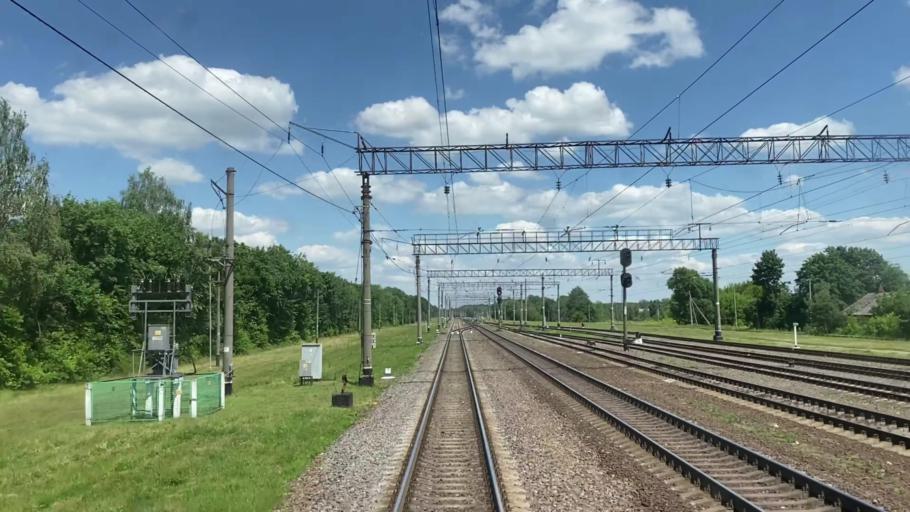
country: BY
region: Brest
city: Zhabinka
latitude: 52.2086
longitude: 24.0359
